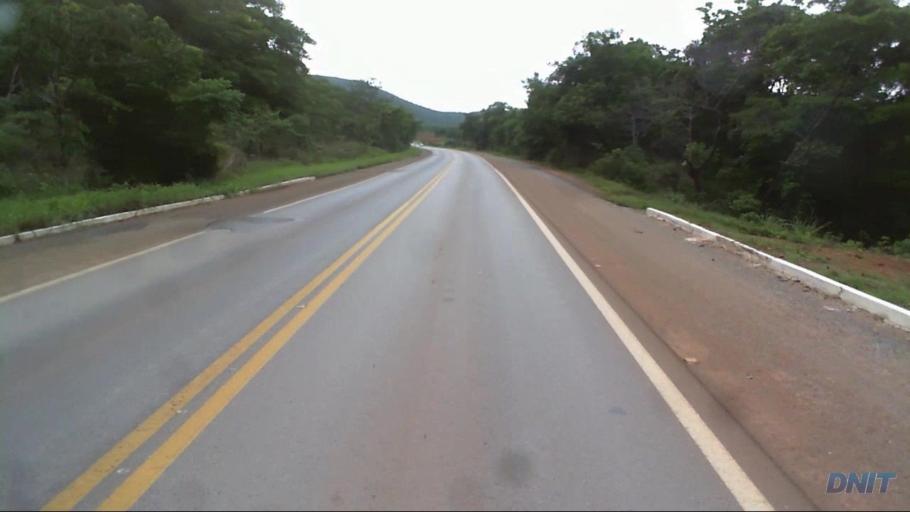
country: BR
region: Goias
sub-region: Barro Alto
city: Barro Alto
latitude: -14.8915
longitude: -48.9748
